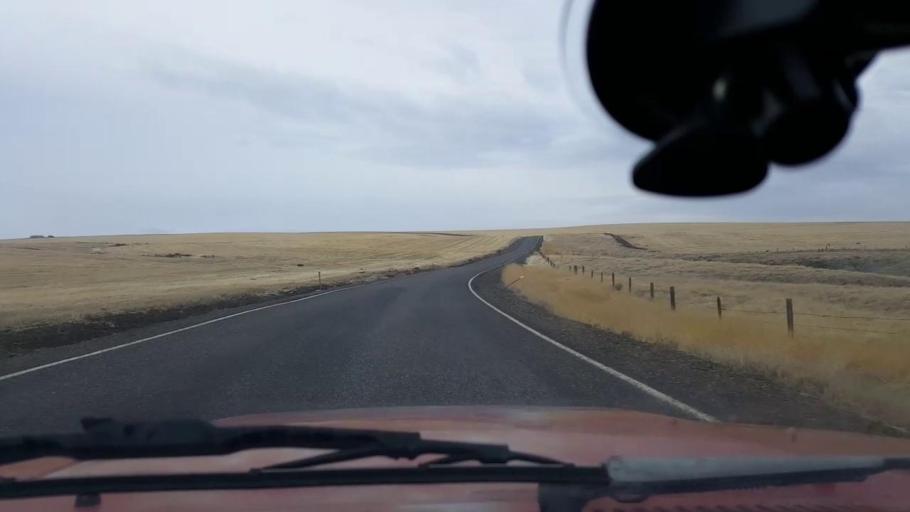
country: US
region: Washington
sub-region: Asotin County
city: Clarkston Heights-Vineland
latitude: 46.3441
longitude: -117.2492
